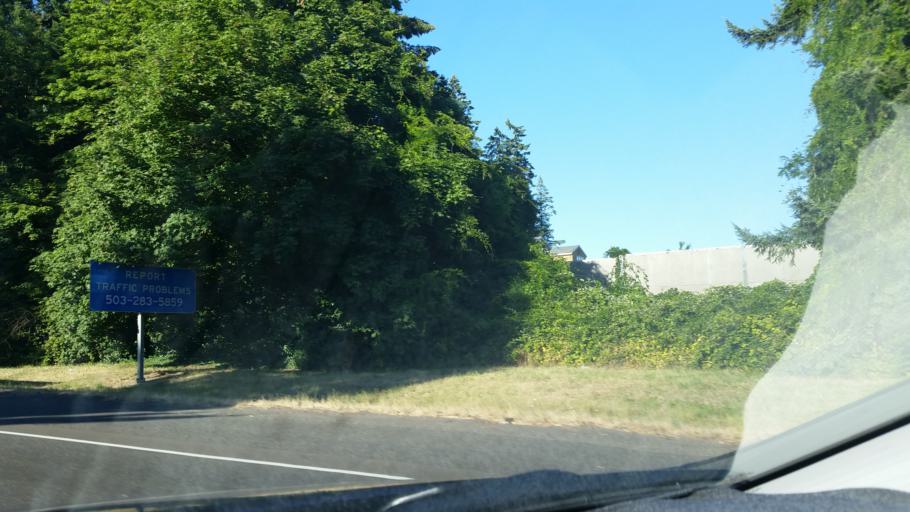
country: US
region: Oregon
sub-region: Clackamas County
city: Wilsonville
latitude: 45.3106
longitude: -122.7691
